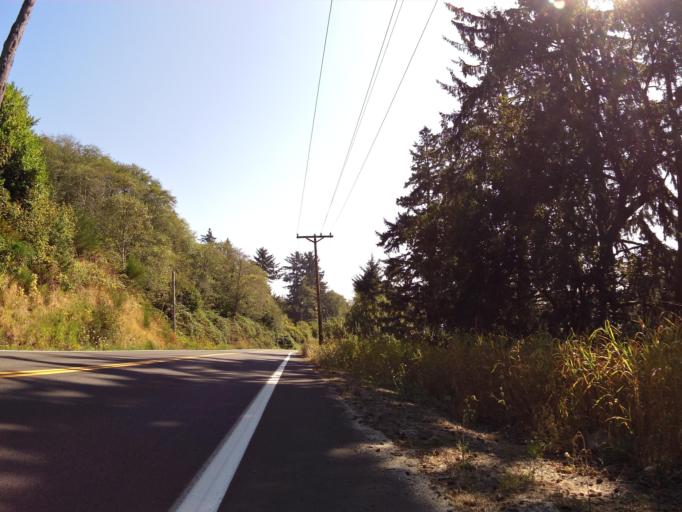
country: US
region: Oregon
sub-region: Tillamook County
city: Pacific City
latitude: 45.1881
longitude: -123.9480
